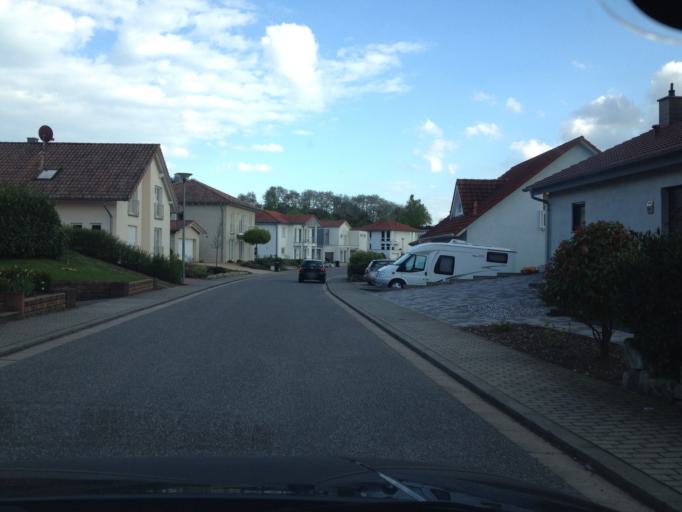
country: DE
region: Saarland
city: Ottweiler
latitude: 49.3993
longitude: 7.1850
